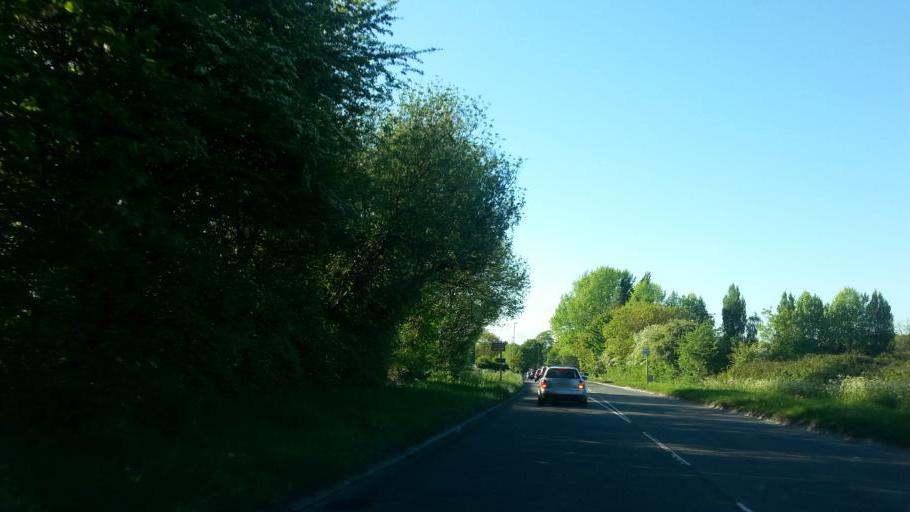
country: GB
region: England
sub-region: Bath and North East Somerset
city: Whitchurch
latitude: 51.3998
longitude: -2.5518
